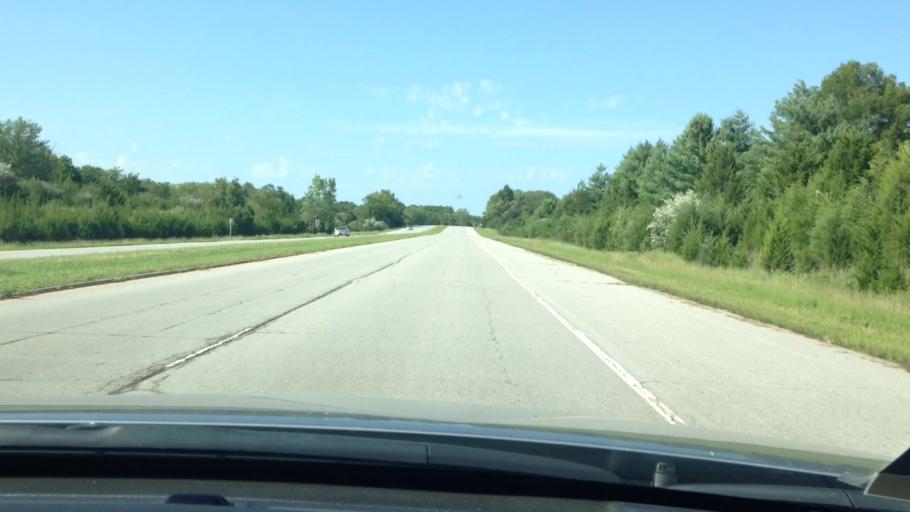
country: US
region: Missouri
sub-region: Jackson County
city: Grandview
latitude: 38.8892
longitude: -94.4940
